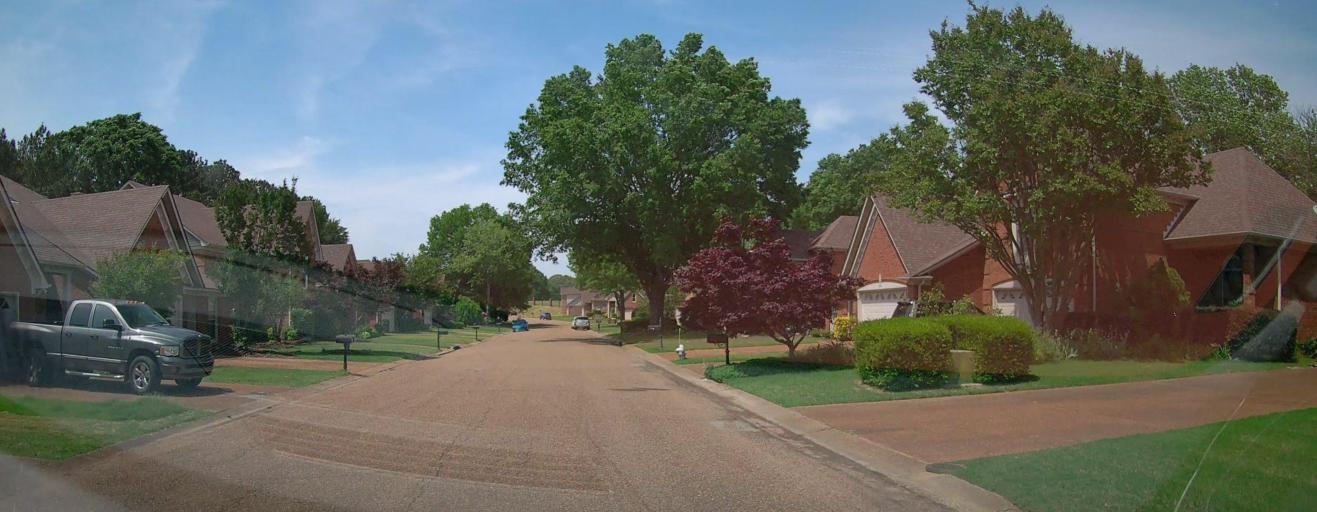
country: US
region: Tennessee
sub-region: Shelby County
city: Germantown
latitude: 35.0398
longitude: -89.7864
